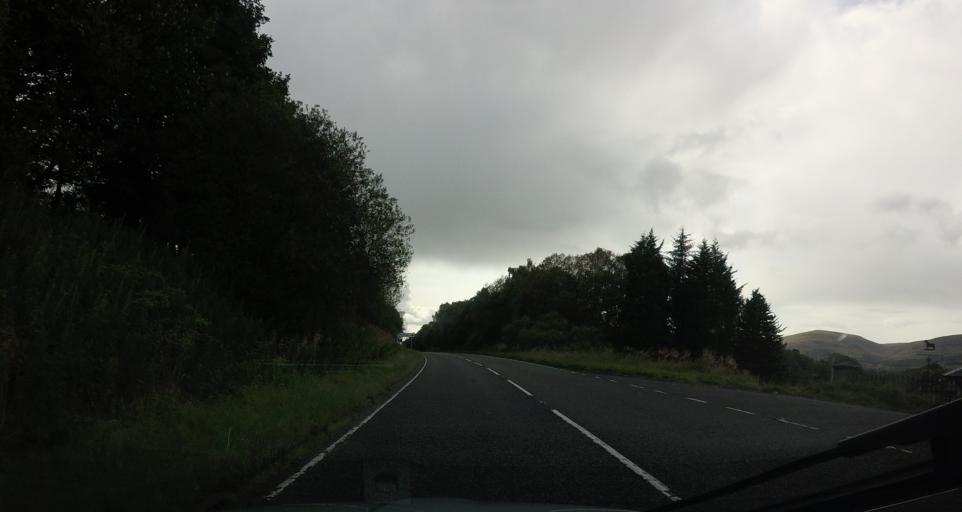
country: GB
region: Scotland
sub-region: Fife
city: Saline
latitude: 56.1608
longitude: -3.6060
